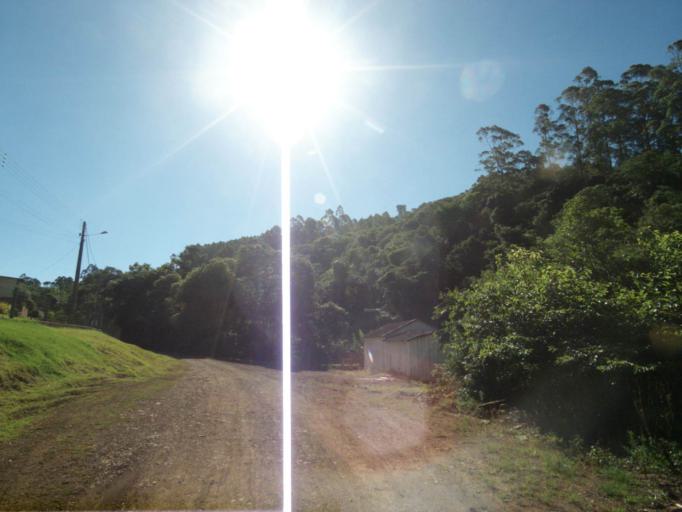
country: BR
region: Parana
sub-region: Ampere
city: Ampere
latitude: -26.1696
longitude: -53.3692
